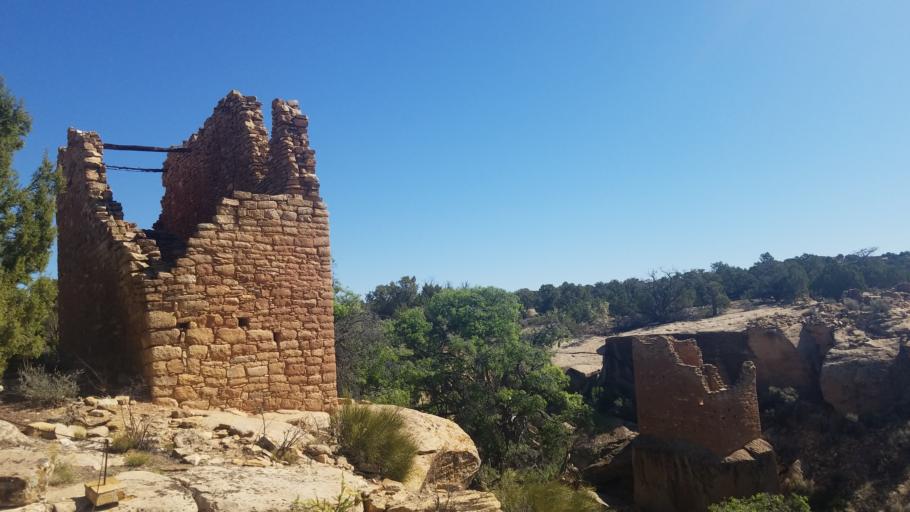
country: US
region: Colorado
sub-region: Montezuma County
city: Towaoc
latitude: 37.3994
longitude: -109.0422
